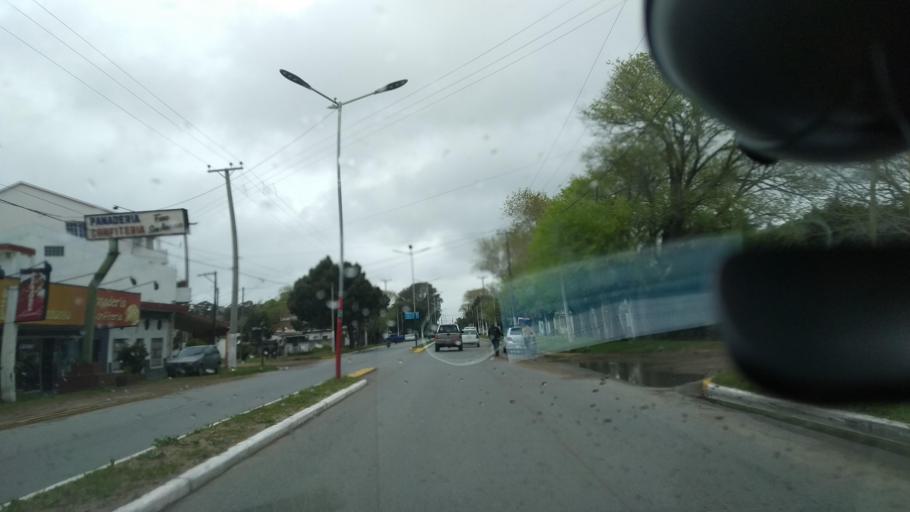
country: AR
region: Buenos Aires
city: San Clemente del Tuyu
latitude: -36.3748
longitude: -56.7187
